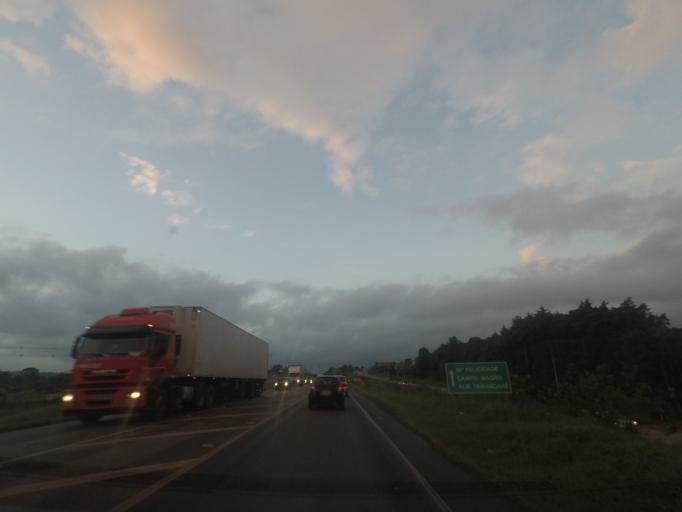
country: BR
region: Parana
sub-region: Curitiba
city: Curitiba
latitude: -25.4052
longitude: -49.3632
